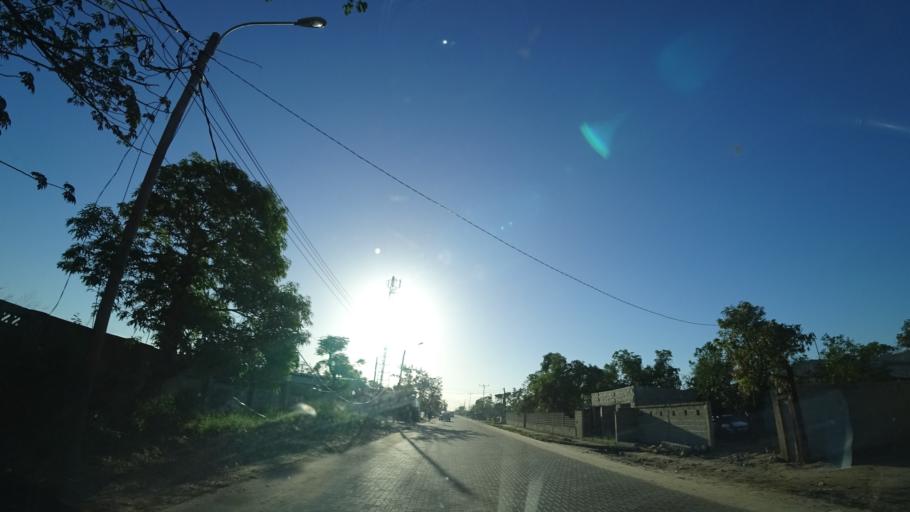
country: MZ
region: Sofala
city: Beira
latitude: -19.7417
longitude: 34.8360
